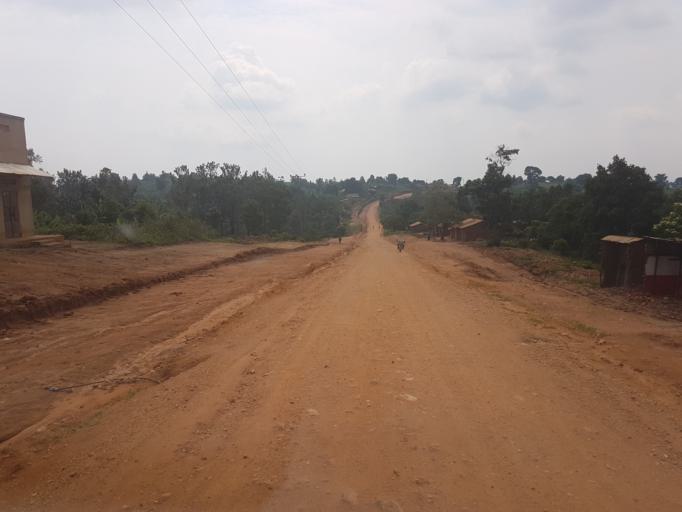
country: UG
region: Western Region
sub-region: Kanungu District
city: Ntungamo
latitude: -0.8202
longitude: 29.7078
